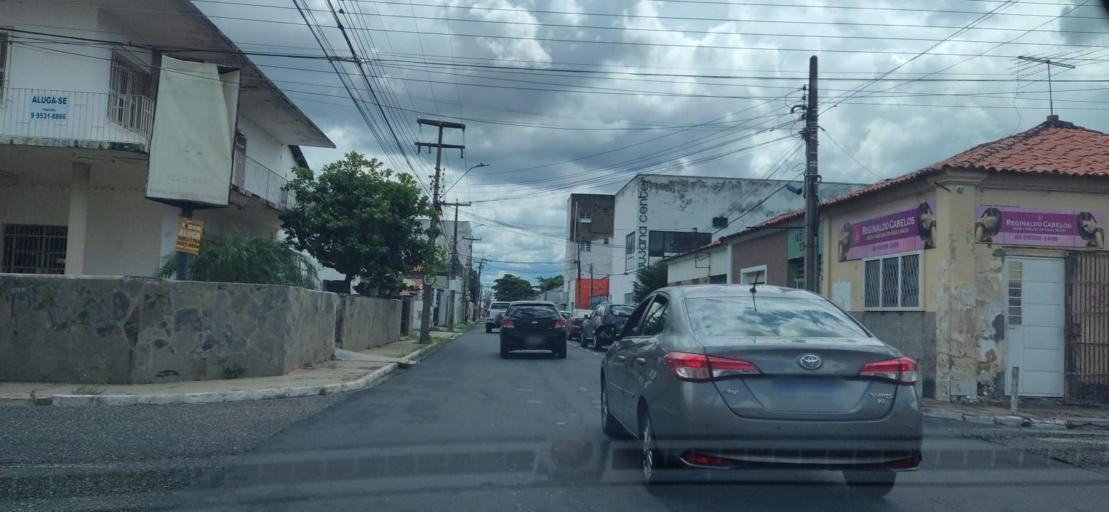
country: BR
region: Piaui
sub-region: Teresina
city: Teresina
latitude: -5.0861
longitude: -42.8120
